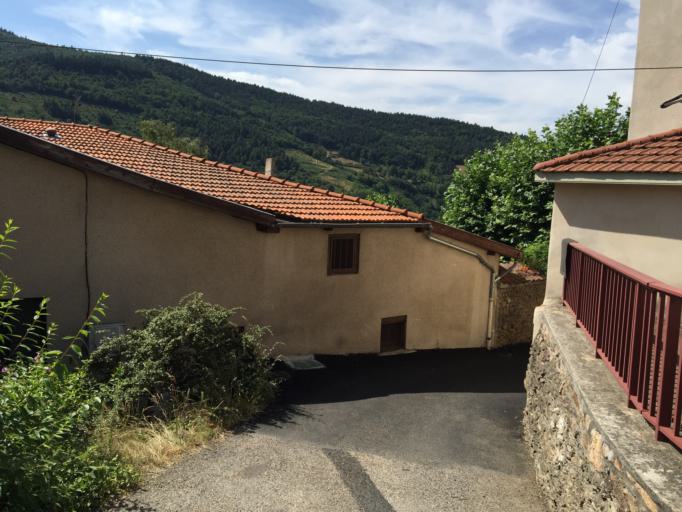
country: FR
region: Rhone-Alpes
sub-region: Departement de la Loire
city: Saint-Chamond
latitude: 45.4164
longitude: 4.5158
